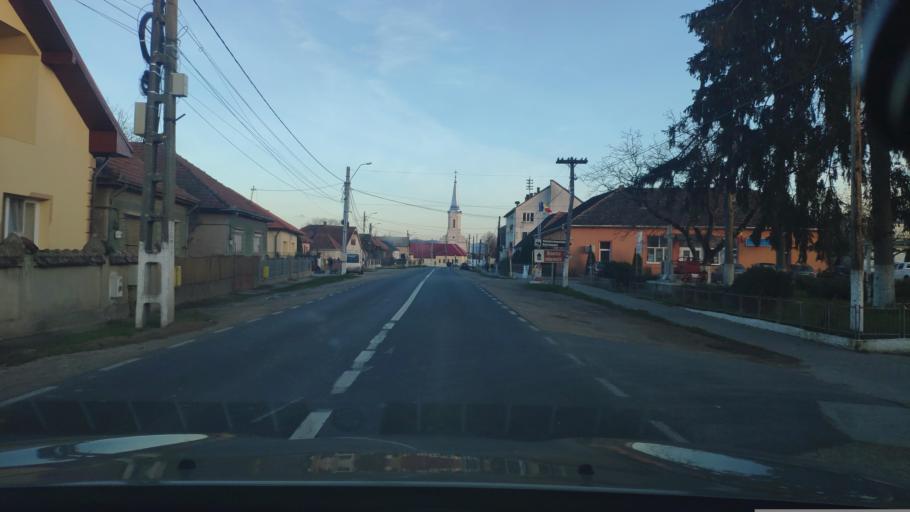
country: RO
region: Satu Mare
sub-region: Comuna Apa
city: Apa
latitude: 47.7632
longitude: 23.1948
